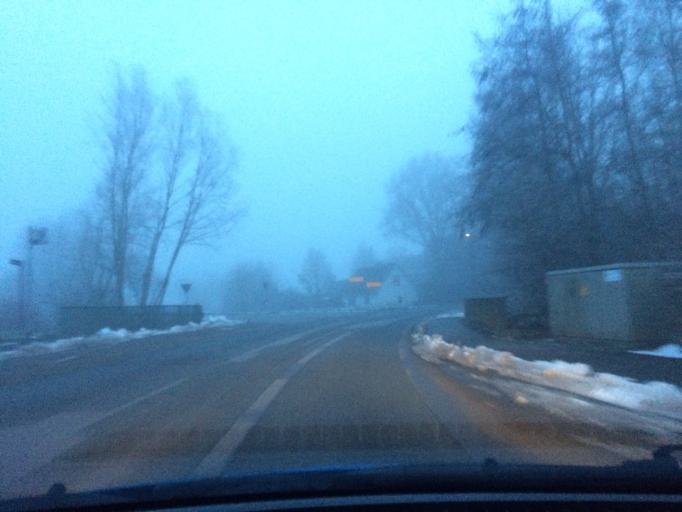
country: DE
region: Schleswig-Holstein
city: Kollow
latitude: 53.4593
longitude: 10.4614
